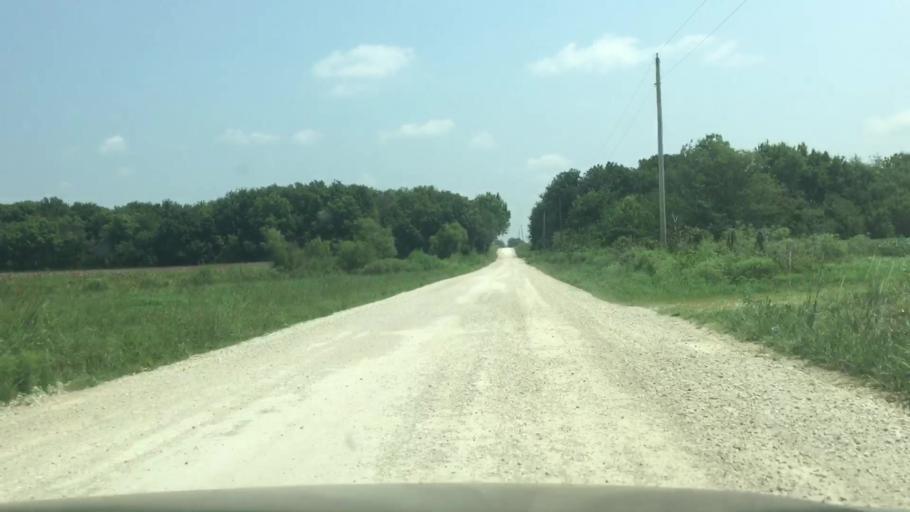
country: US
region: Kansas
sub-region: Allen County
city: Humboldt
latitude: 37.8493
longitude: -95.4003
